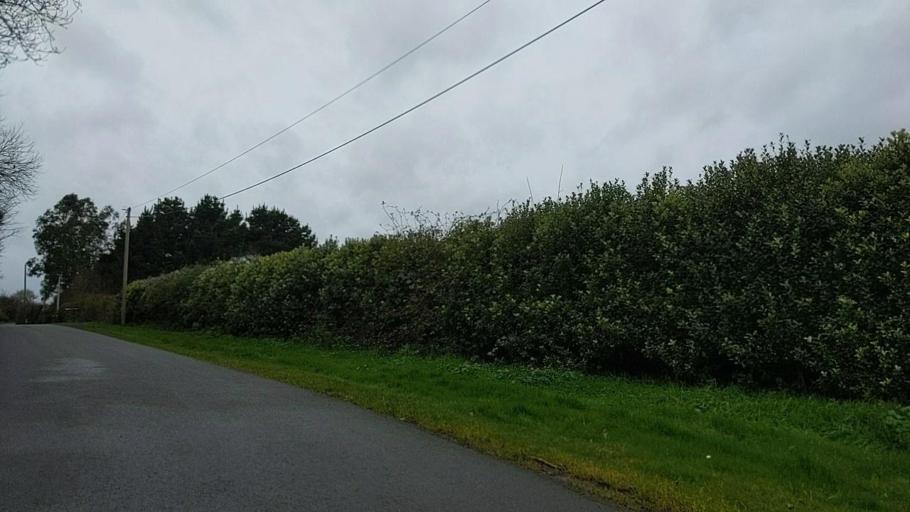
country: FR
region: Brittany
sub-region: Departement des Cotes-d'Armor
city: Pleumeur-Gautier
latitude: 48.8352
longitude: -3.1822
